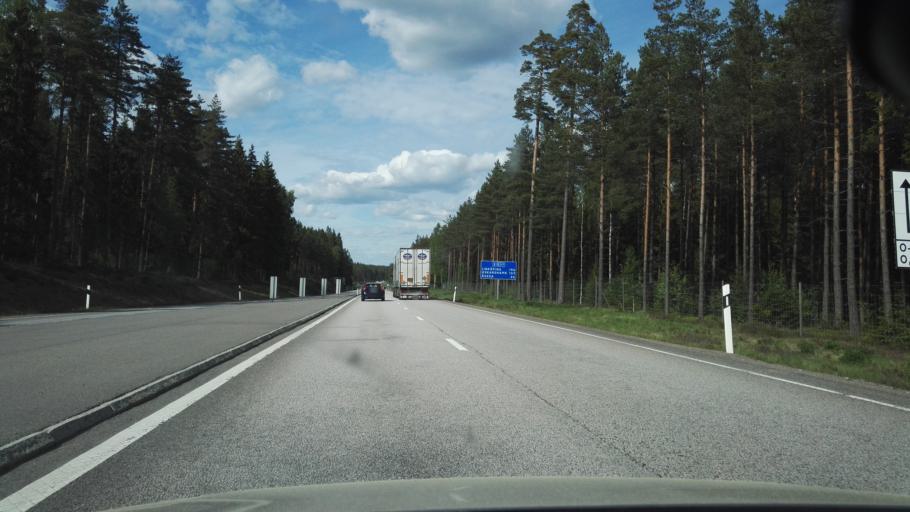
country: SE
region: Kronoberg
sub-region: Vaxjo Kommun
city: Braas
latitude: 57.0187
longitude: 15.0554
